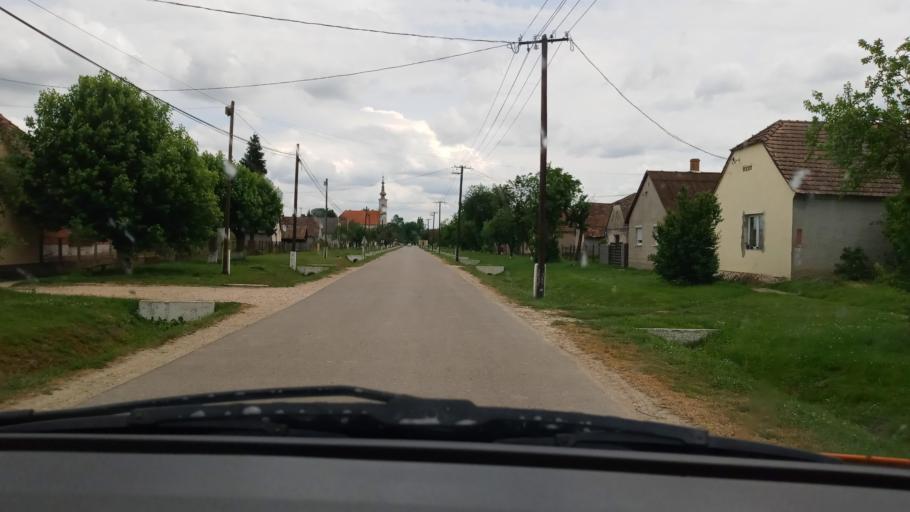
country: HU
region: Baranya
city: Vajszlo
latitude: 45.8268
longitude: 17.9895
